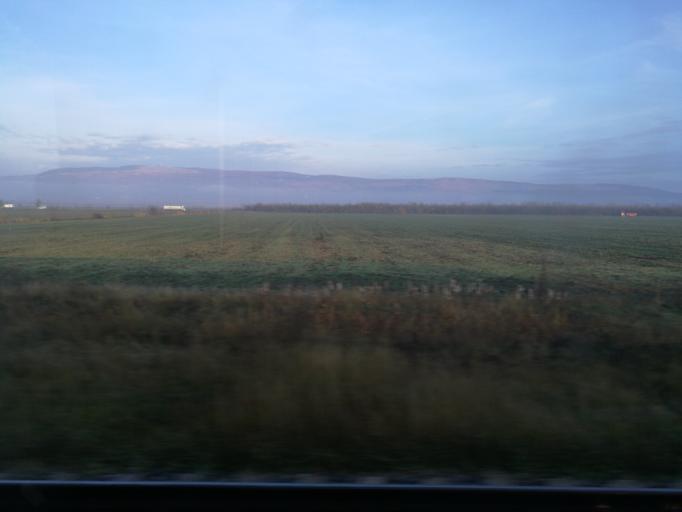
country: RO
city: Valcele
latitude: 45.0690
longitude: 26.6200
